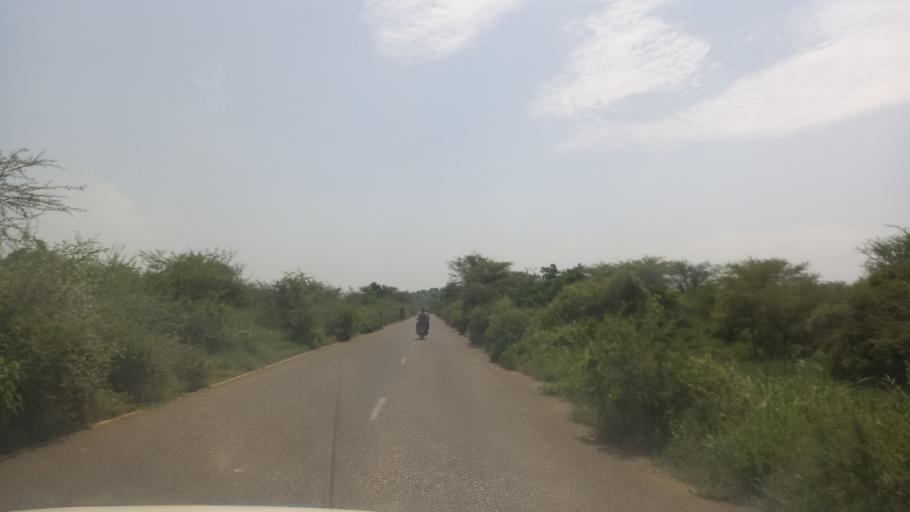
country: ET
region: Gambela
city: Gambela
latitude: 8.2811
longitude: 34.2235
